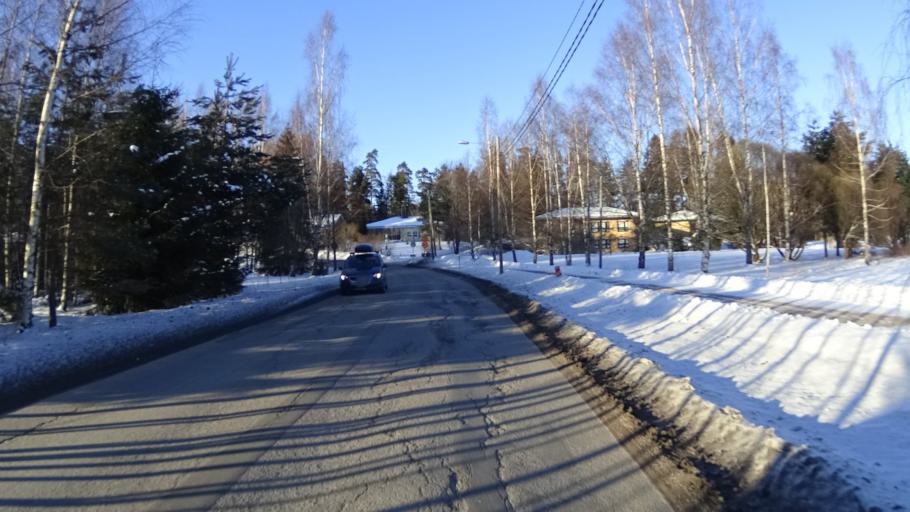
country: FI
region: Uusimaa
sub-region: Helsinki
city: Espoo
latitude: 60.2348
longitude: 24.6584
